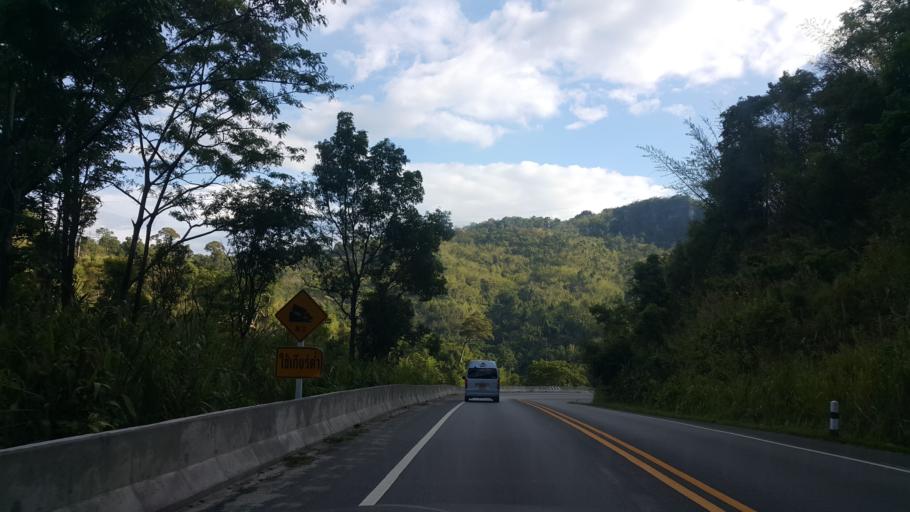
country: TH
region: Phayao
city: Phayao
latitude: 19.0713
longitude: 99.7706
